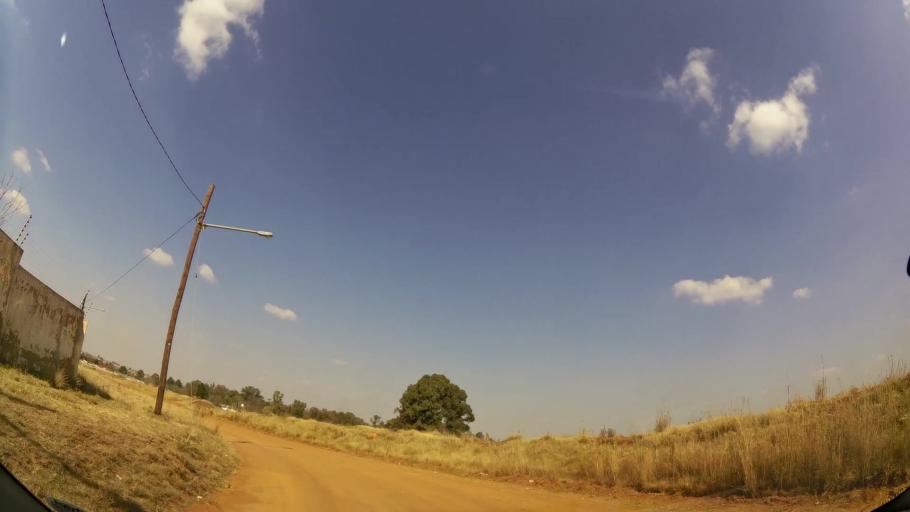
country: ZA
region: Gauteng
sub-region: Ekurhuleni Metropolitan Municipality
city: Benoni
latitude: -26.0990
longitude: 28.4061
